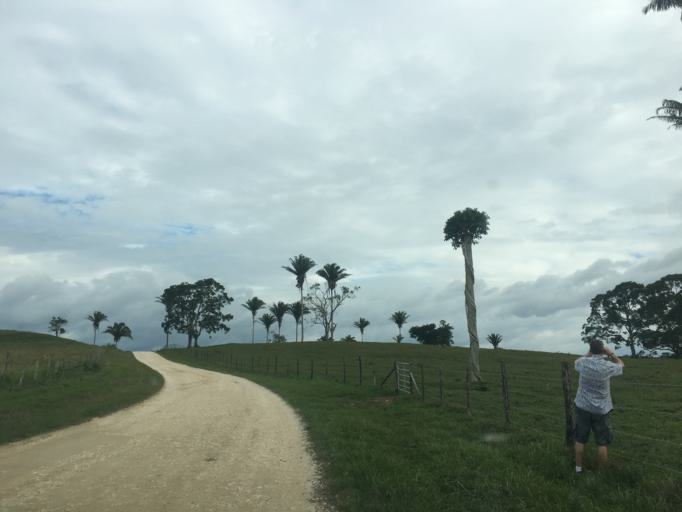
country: BZ
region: Cayo
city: Benque Viejo del Carmen
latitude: 17.1121
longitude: -89.1255
